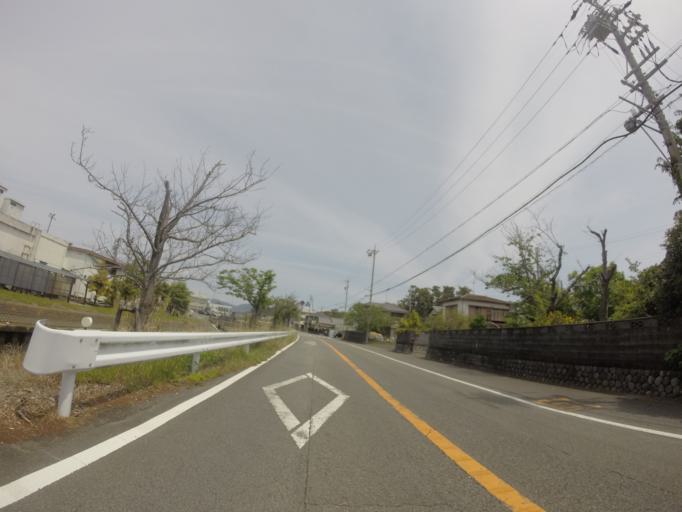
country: JP
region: Shizuoka
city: Yaizu
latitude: 34.8289
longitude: 138.3347
